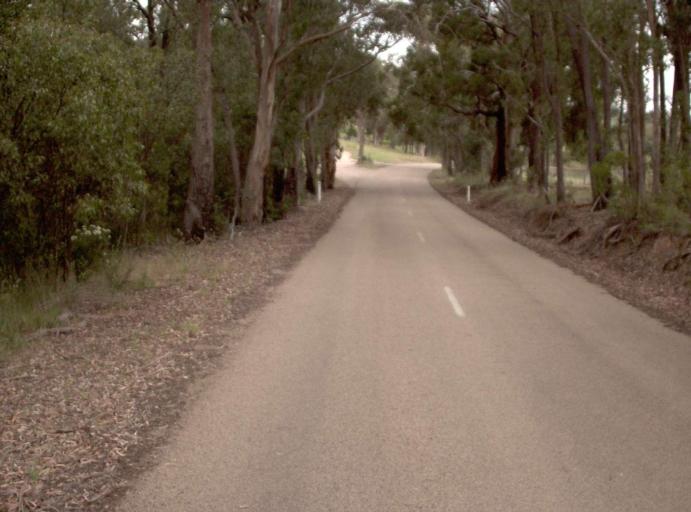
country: AU
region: Victoria
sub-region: East Gippsland
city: Bairnsdale
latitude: -37.7312
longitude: 147.5912
